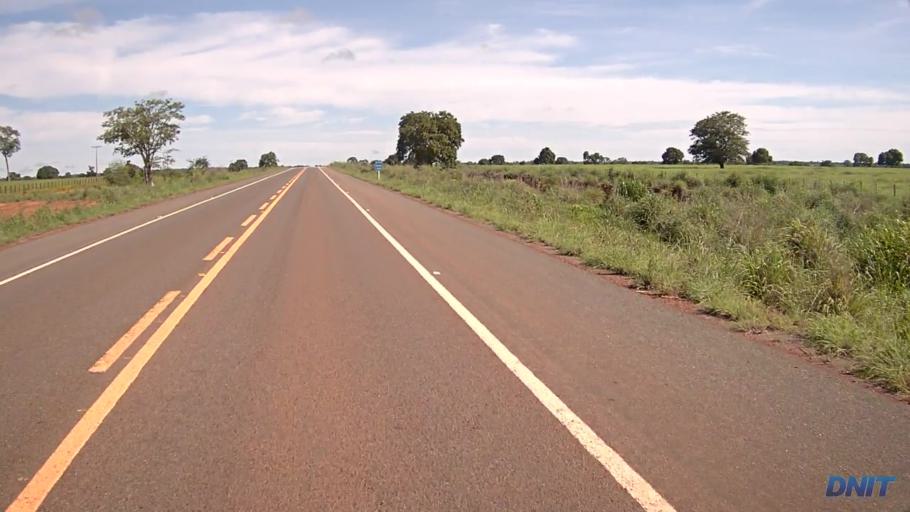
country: BR
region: Goias
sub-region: Sao Miguel Do Araguaia
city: Sao Miguel do Araguaia
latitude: -13.3732
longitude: -50.1430
